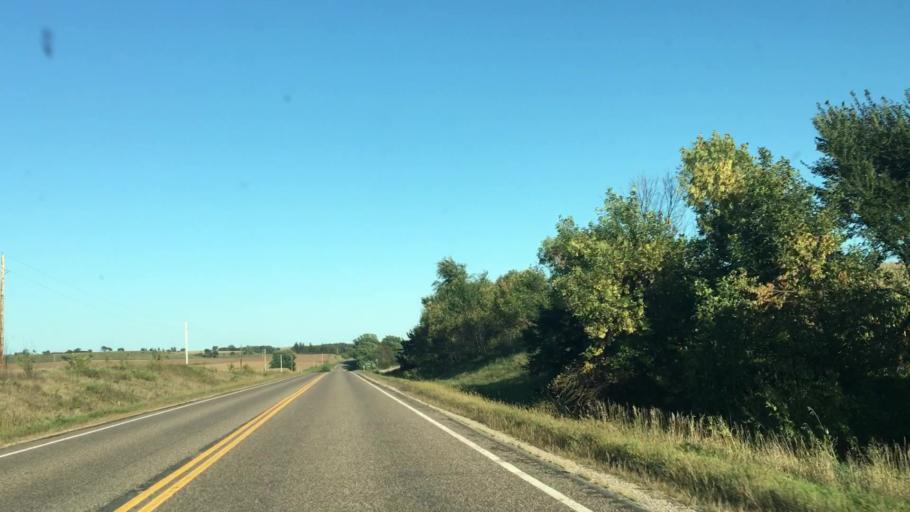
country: US
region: Minnesota
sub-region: Fillmore County
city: Chatfield
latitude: 43.8542
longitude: -92.1326
